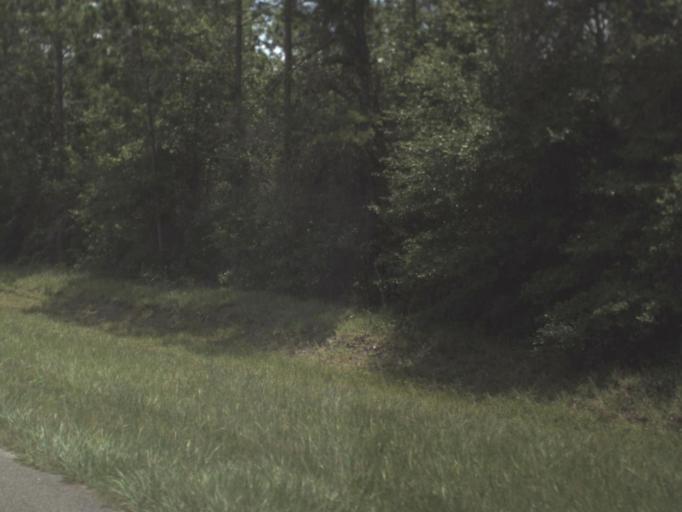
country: US
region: Florida
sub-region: Union County
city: Lake Butler
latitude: 29.9930
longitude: -82.3516
